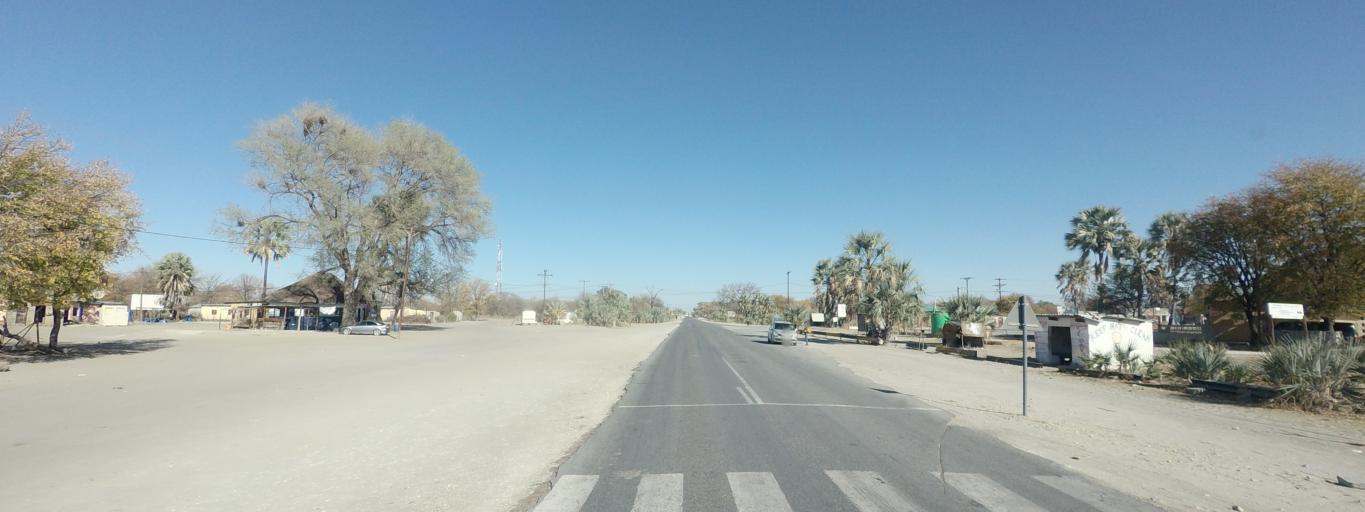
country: BW
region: Central
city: Nata
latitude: -20.2160
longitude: 26.1895
